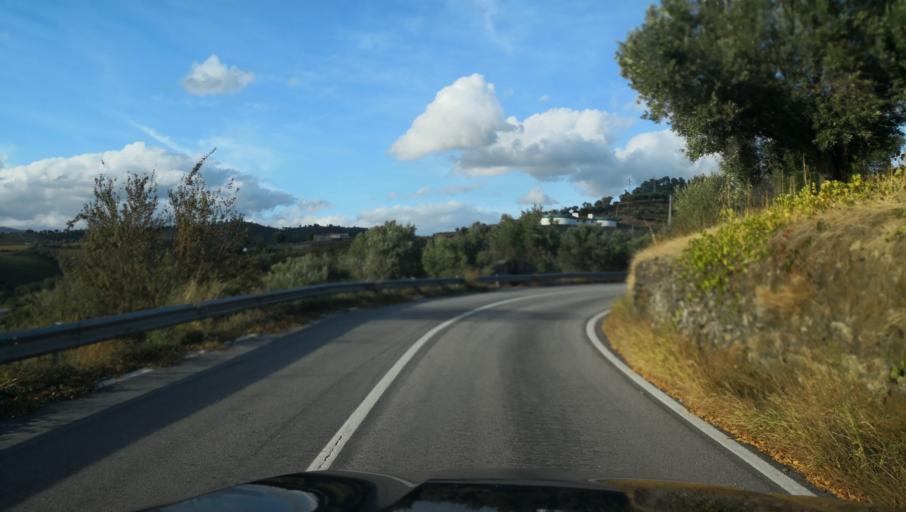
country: PT
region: Vila Real
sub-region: Peso da Regua
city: Peso da Regua
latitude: 41.1715
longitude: -7.7772
